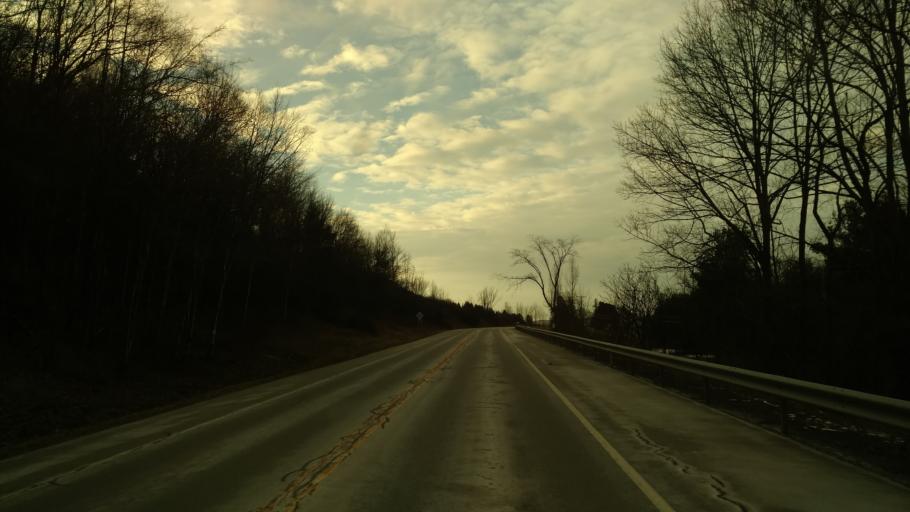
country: US
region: New York
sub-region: Allegany County
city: Wellsville
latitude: 42.0718
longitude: -77.9193
